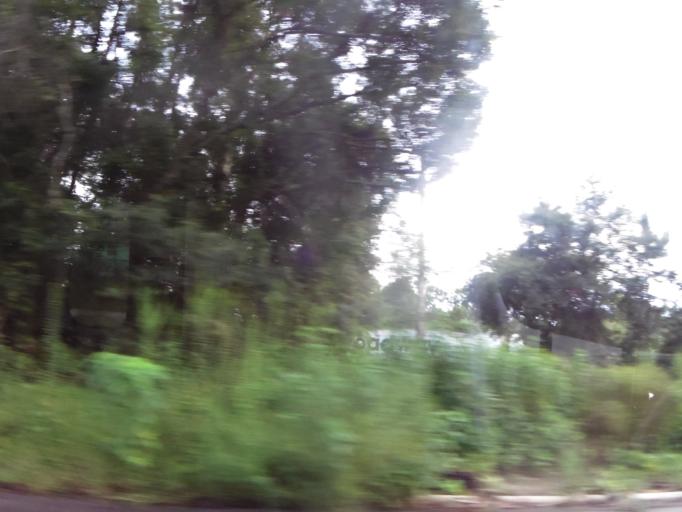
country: US
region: Florida
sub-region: Duval County
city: Jacksonville
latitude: 30.3580
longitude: -81.7100
